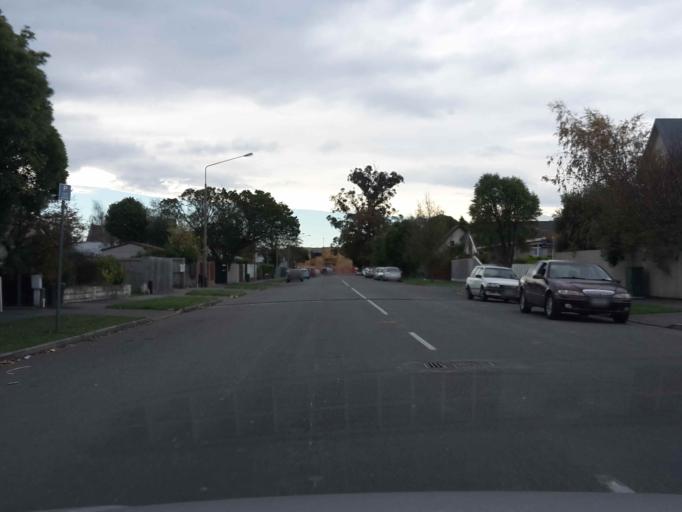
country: NZ
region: Canterbury
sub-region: Christchurch City
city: Christchurch
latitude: -43.5315
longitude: 172.6064
